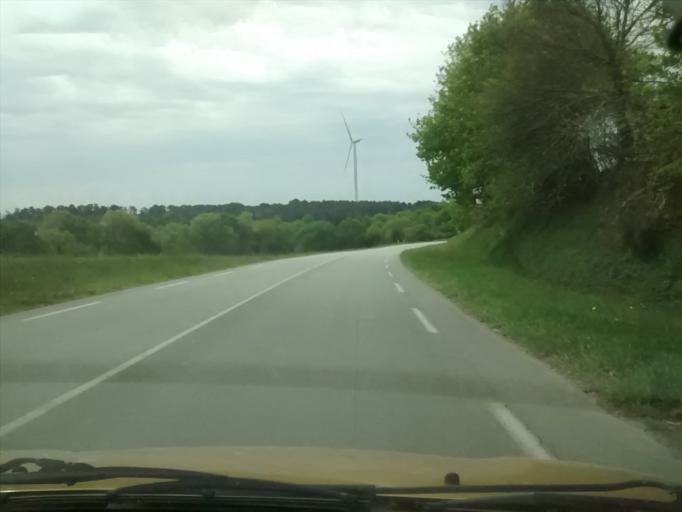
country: FR
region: Brittany
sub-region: Departement du Morbihan
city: Berric
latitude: 47.6086
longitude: -2.5409
